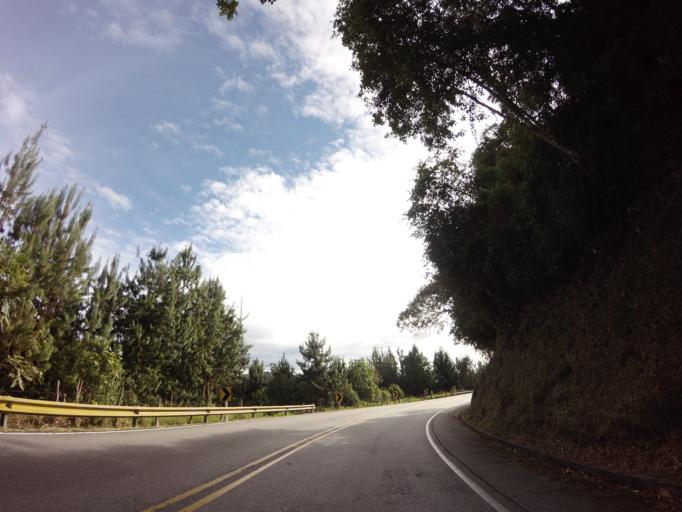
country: CO
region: Tolima
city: Herveo
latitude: 5.1461
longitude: -75.1546
